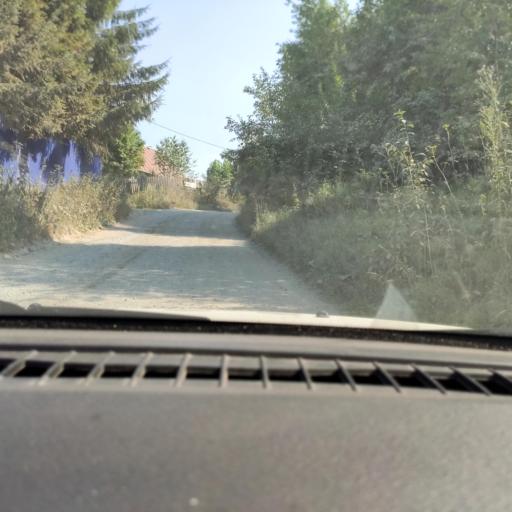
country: RU
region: Perm
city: Polazna
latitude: 58.1401
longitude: 56.4570
